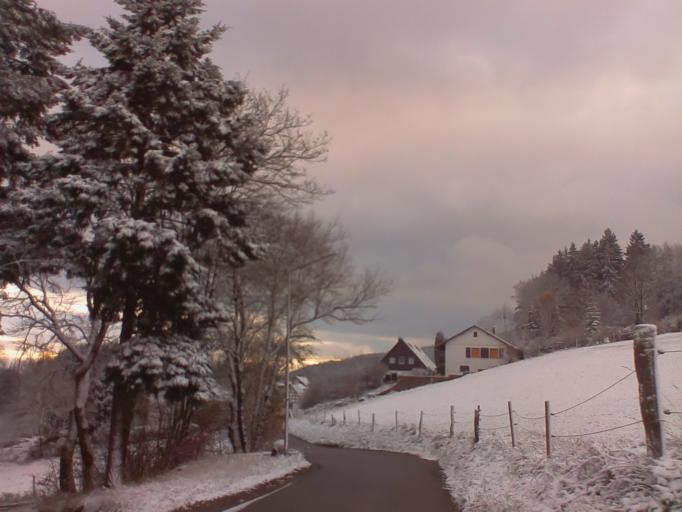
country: DE
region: Hesse
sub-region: Regierungsbezirk Darmstadt
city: Wald-Michelbach
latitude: 49.5583
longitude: 8.8324
